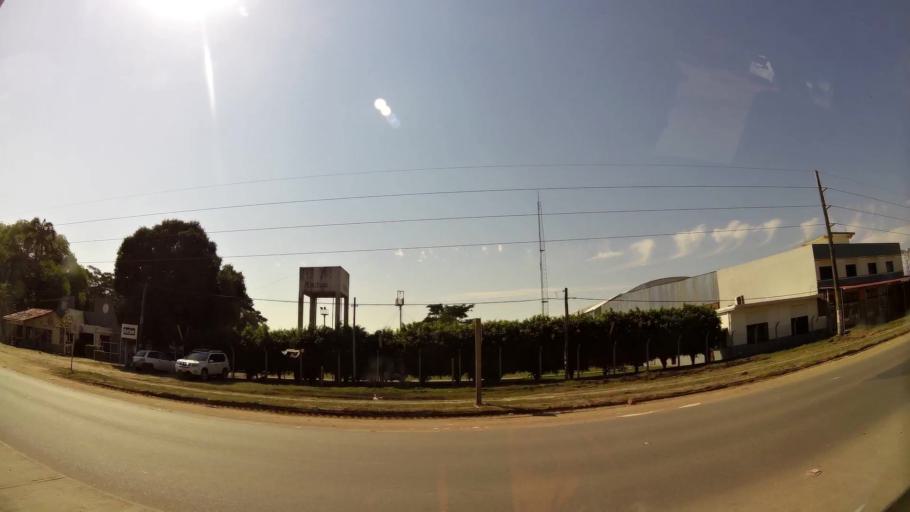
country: BO
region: Santa Cruz
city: Cotoca
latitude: -17.7648
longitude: -63.0910
